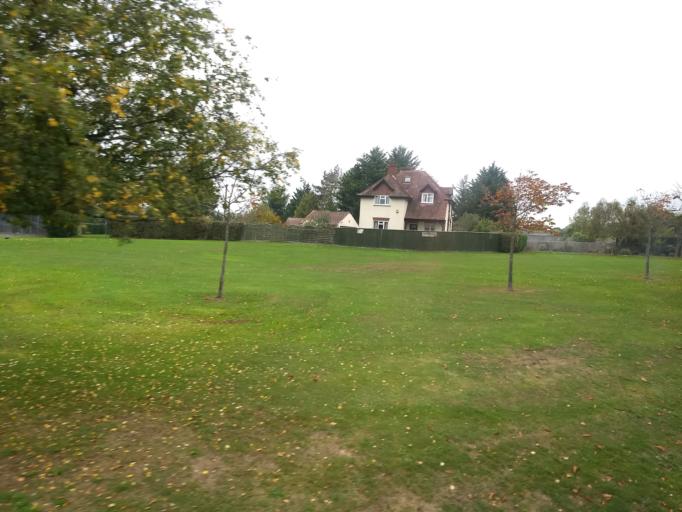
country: GB
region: England
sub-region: Isle of Wight
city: Newport
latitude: 50.7060
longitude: -1.2858
